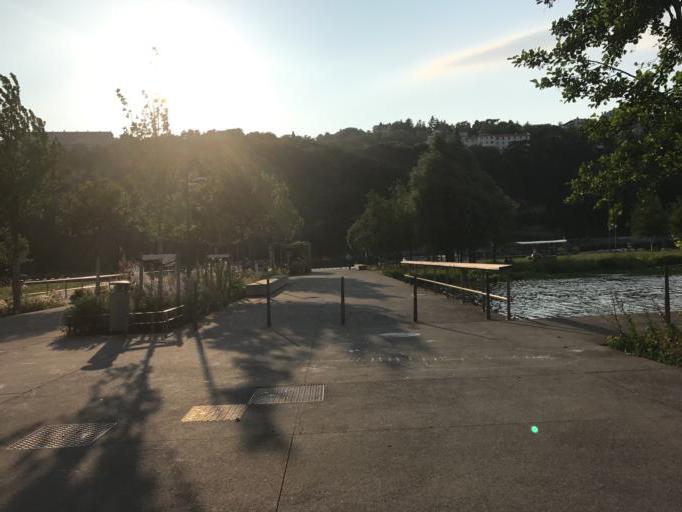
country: FR
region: Rhone-Alpes
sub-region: Departement du Rhone
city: La Mulatiere
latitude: 45.7431
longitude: 4.8157
